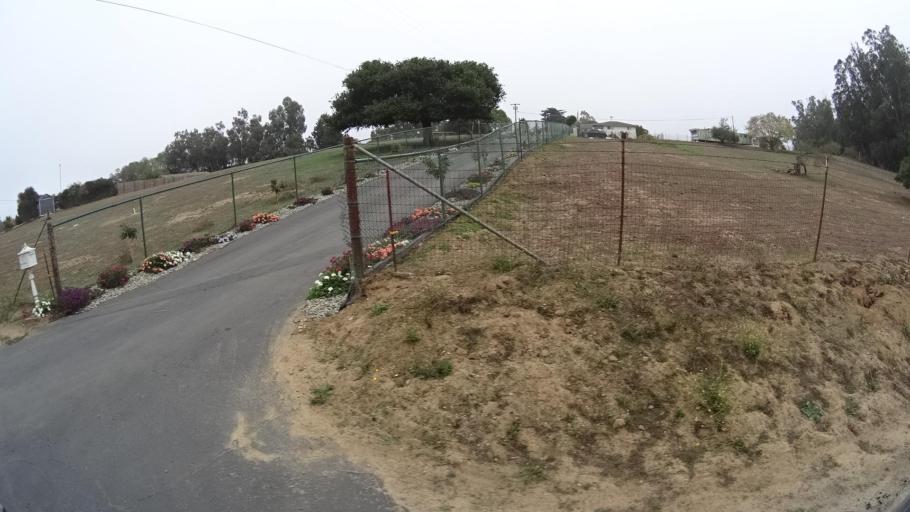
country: US
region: California
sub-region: Monterey County
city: Las Lomas
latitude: 36.8704
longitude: -121.6945
